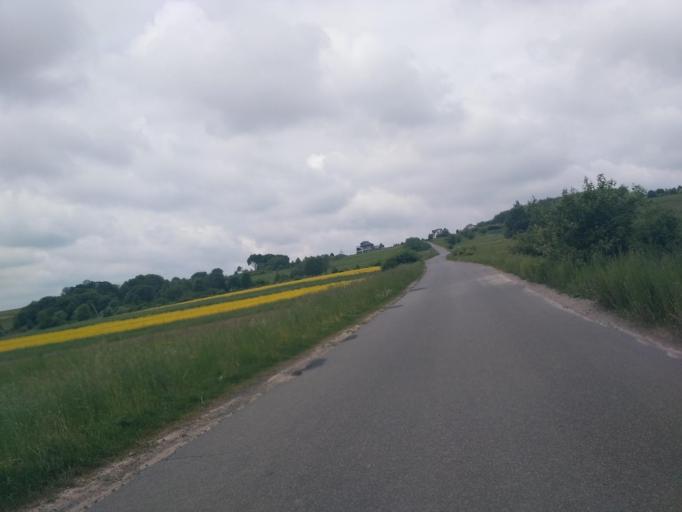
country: PL
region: Subcarpathian Voivodeship
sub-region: Powiat krosnienski
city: Chorkowka
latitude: 49.6704
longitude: 21.6727
